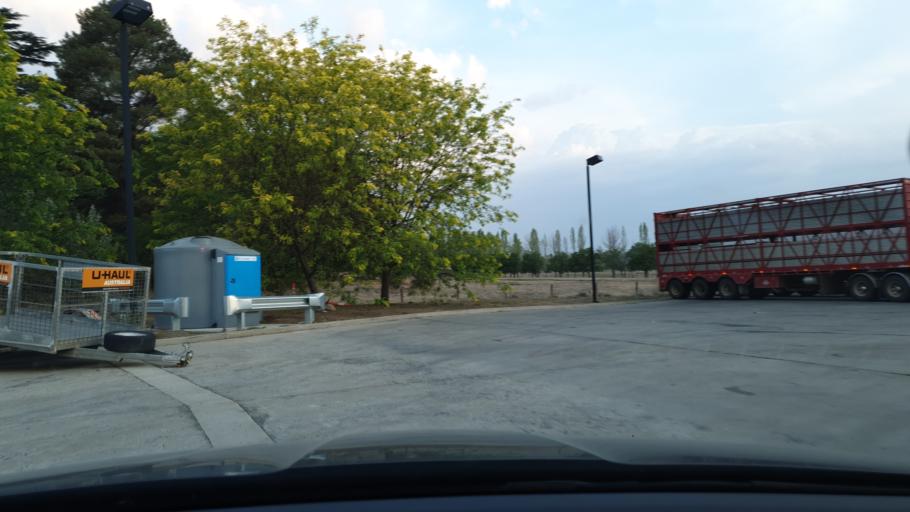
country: AU
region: New South Wales
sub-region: Glen Innes Severn
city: Glen Innes
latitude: -29.7271
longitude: 151.7409
